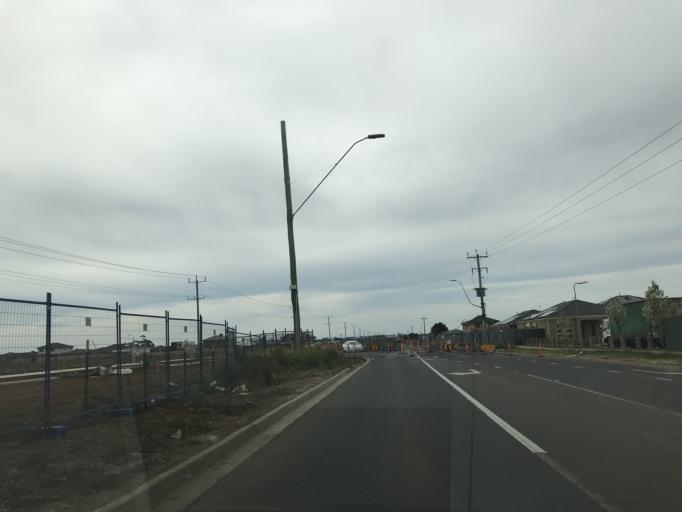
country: AU
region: Victoria
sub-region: Wyndham
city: Williams Landing
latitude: -37.8371
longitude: 144.7198
